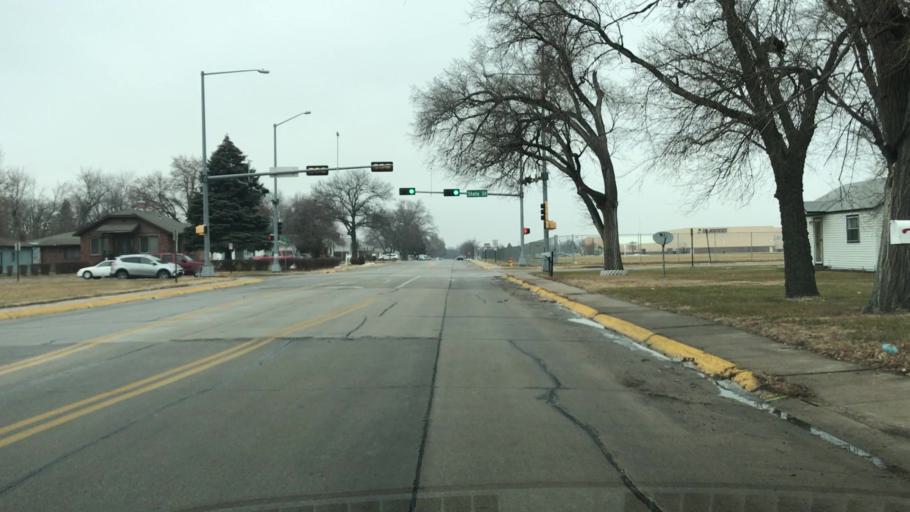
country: US
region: Nebraska
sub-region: Hall County
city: Grand Island
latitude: 40.9380
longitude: -98.3684
